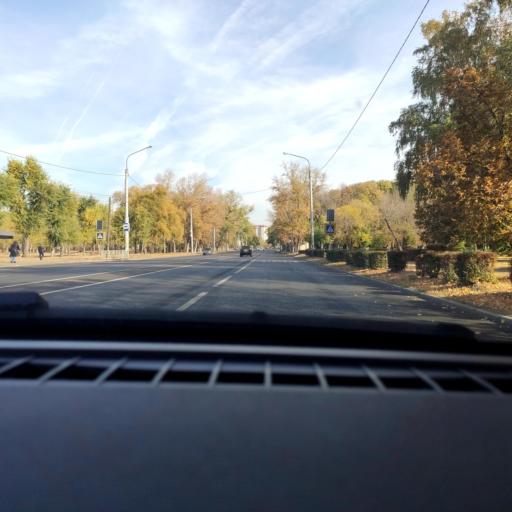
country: RU
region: Voronezj
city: Maslovka
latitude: 51.6064
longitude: 39.2442
